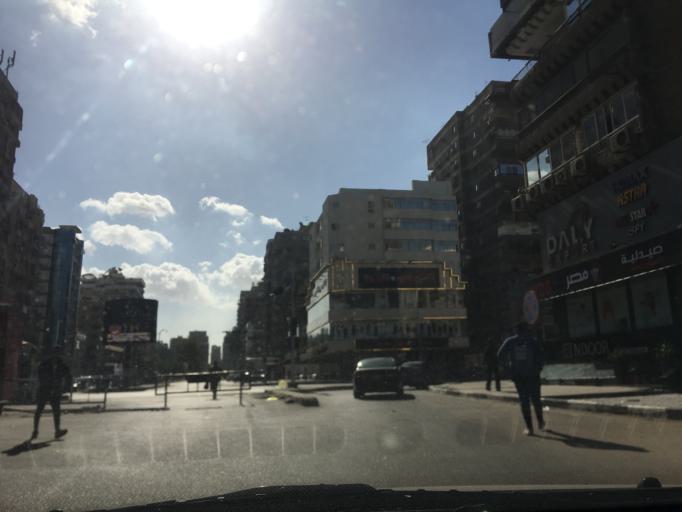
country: EG
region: Muhafazat al Qahirah
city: Cairo
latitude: 30.0551
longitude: 31.3460
